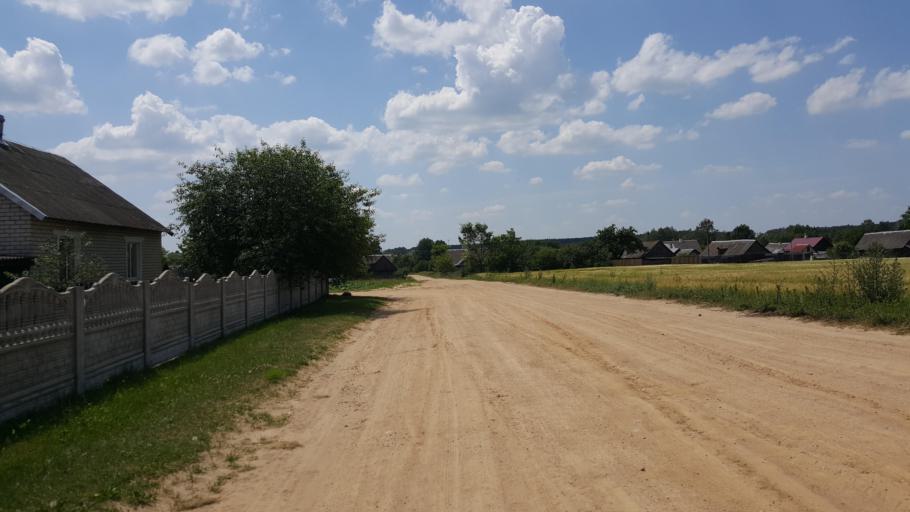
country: BY
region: Brest
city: Kamyanyets
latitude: 52.3989
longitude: 23.7601
